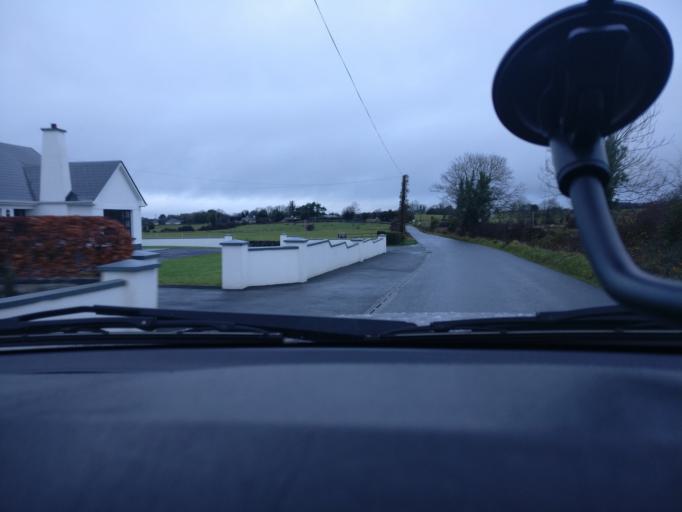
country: IE
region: Connaught
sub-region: County Galway
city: Loughrea
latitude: 53.2567
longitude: -8.5842
